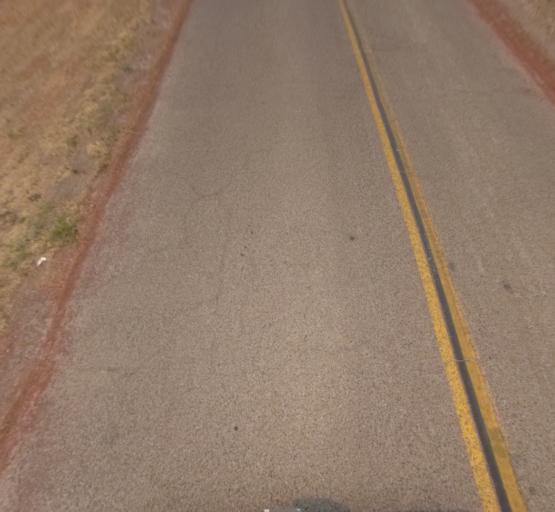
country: US
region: California
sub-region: Madera County
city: Madera Acres
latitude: 37.0149
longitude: -120.0703
